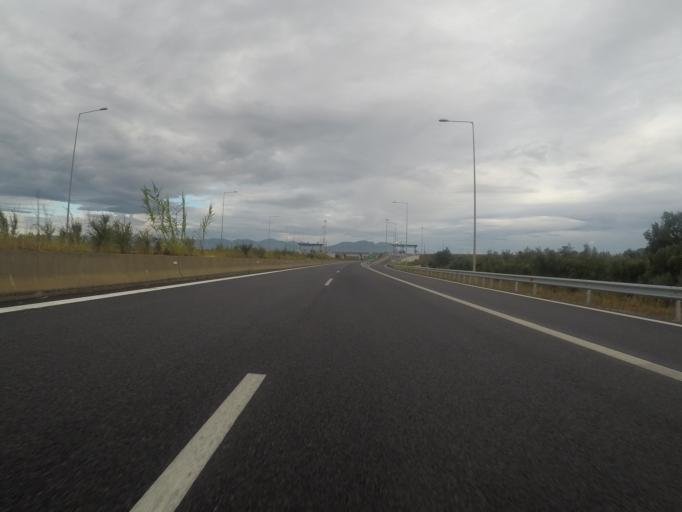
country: GR
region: Peloponnese
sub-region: Nomos Messinias
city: Thouria
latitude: 37.0697
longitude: 22.0503
